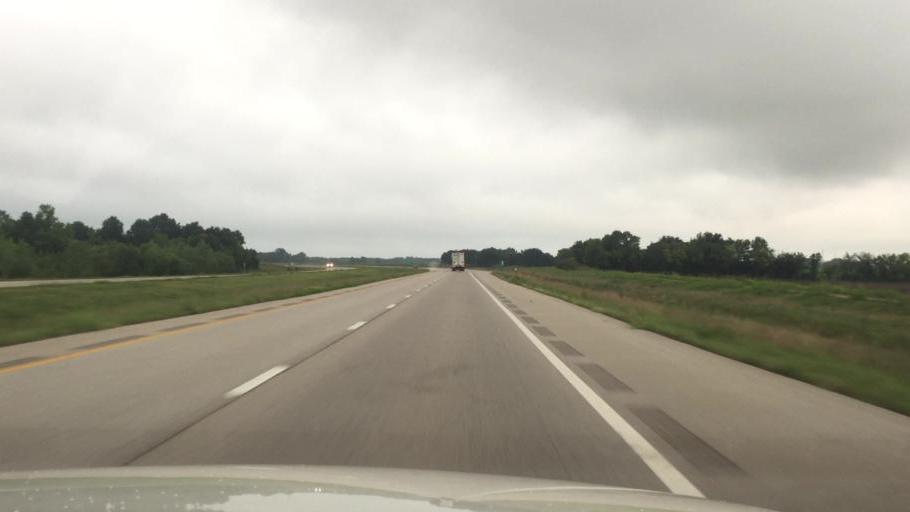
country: US
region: Kansas
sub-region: Montgomery County
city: Coffeyville
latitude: 37.0820
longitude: -95.5899
